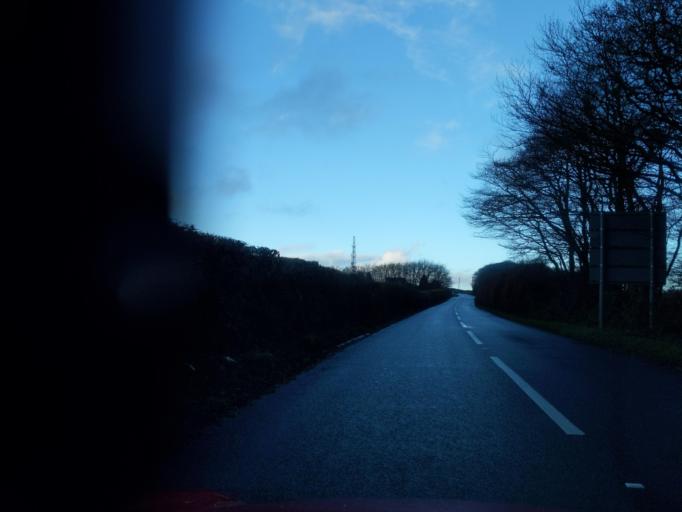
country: GB
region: England
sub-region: Devon
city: Okehampton
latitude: 50.7330
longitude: -4.0356
